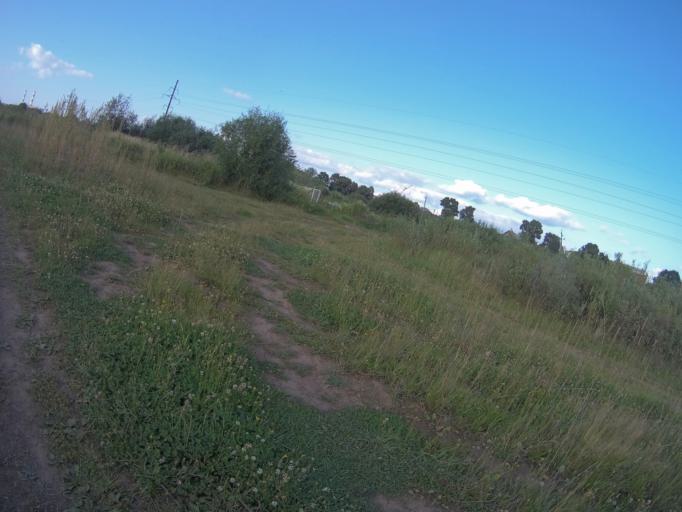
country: RU
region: Vladimir
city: Kommunar
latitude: 56.1232
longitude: 40.4547
